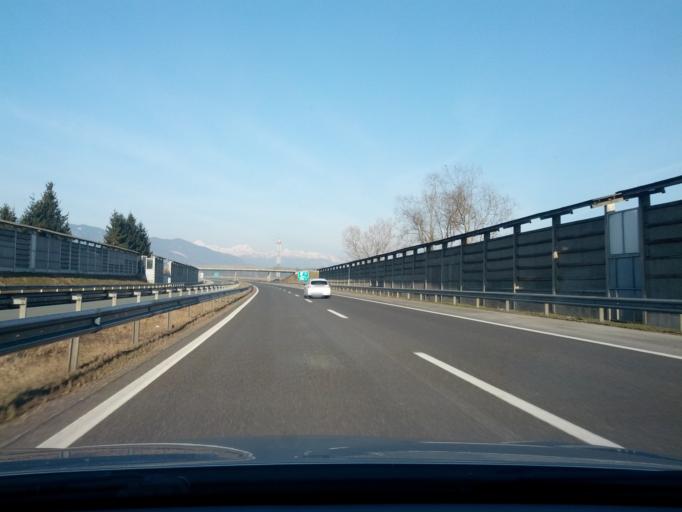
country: SI
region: Naklo
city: Naklo
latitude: 46.2764
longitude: 14.3171
